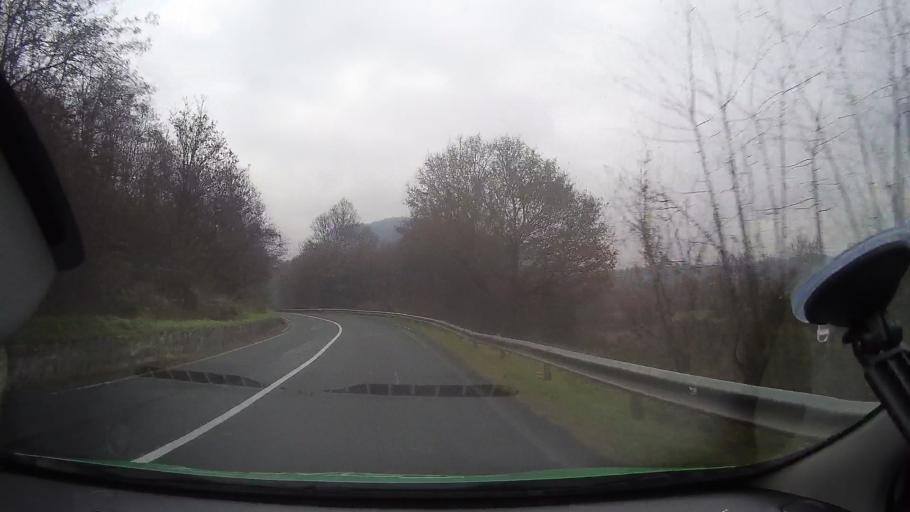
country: RO
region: Arad
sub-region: Comuna Plescuta
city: Plescuta
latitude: 46.2951
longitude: 22.4400
